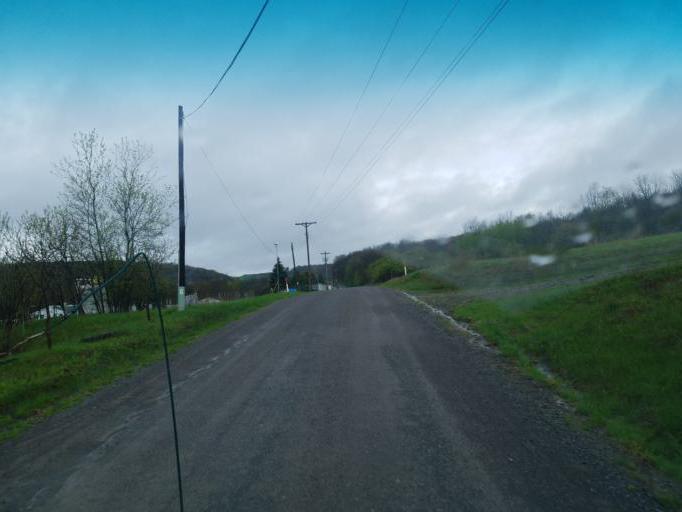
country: US
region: Pennsylvania
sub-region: Tioga County
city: Westfield
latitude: 41.9795
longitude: -77.6847
